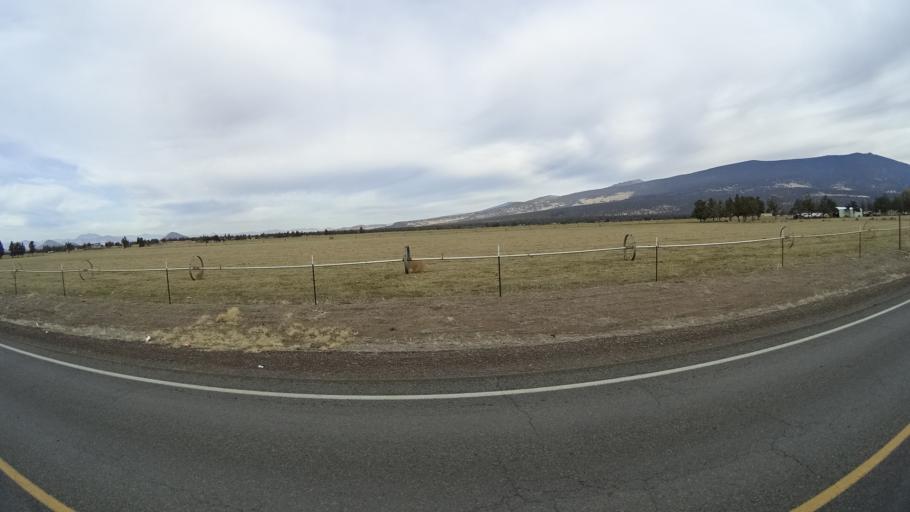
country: US
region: California
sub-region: Siskiyou County
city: Weed
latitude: 41.5963
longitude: -122.3381
